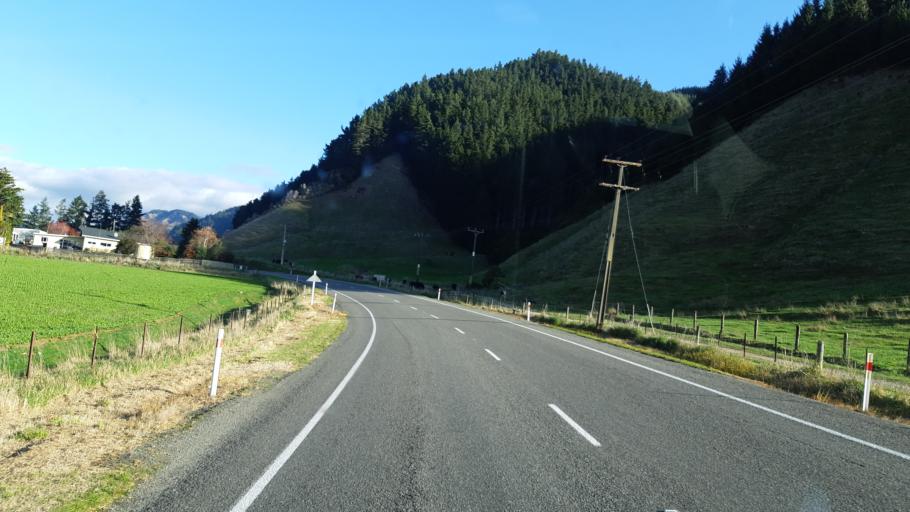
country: NZ
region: Marlborough
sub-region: Marlborough District
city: Picton
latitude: -41.3058
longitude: 173.7683
